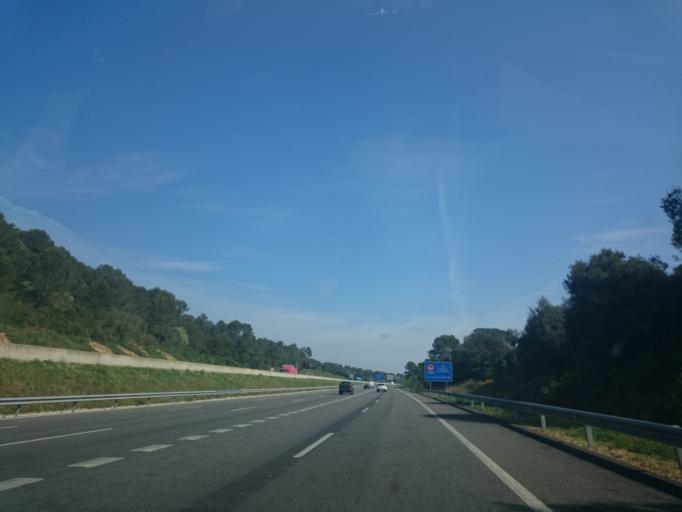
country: ES
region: Catalonia
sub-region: Provincia de Girona
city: Cervia de Ter
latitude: 42.0669
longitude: 2.8868
